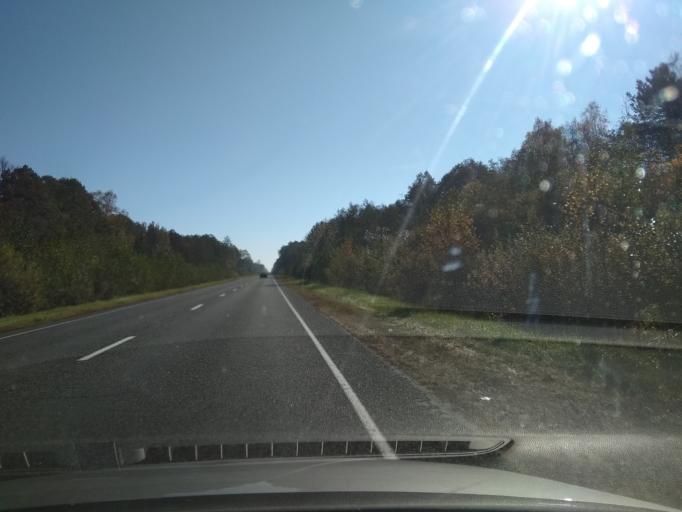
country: BY
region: Brest
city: Malaryta
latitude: 51.9187
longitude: 24.0865
